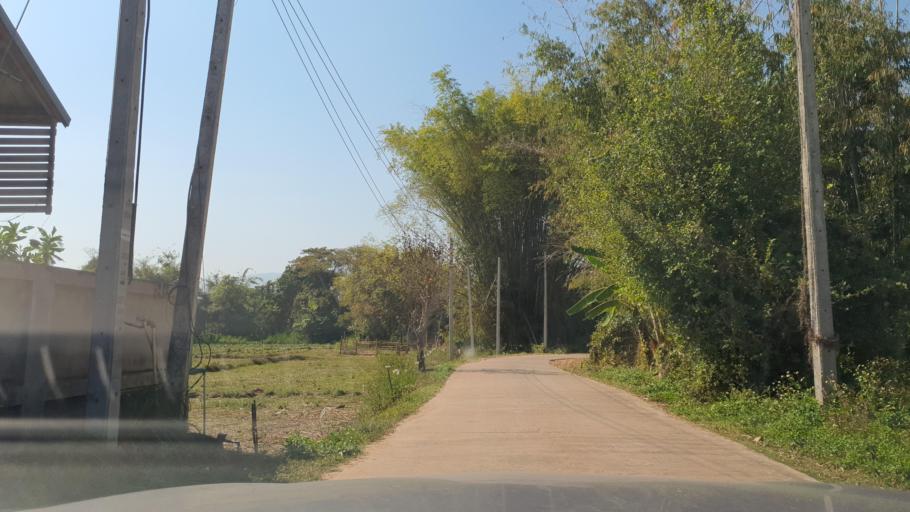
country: TH
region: Chiang Rai
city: Mae Lao
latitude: 19.7986
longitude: 99.7023
